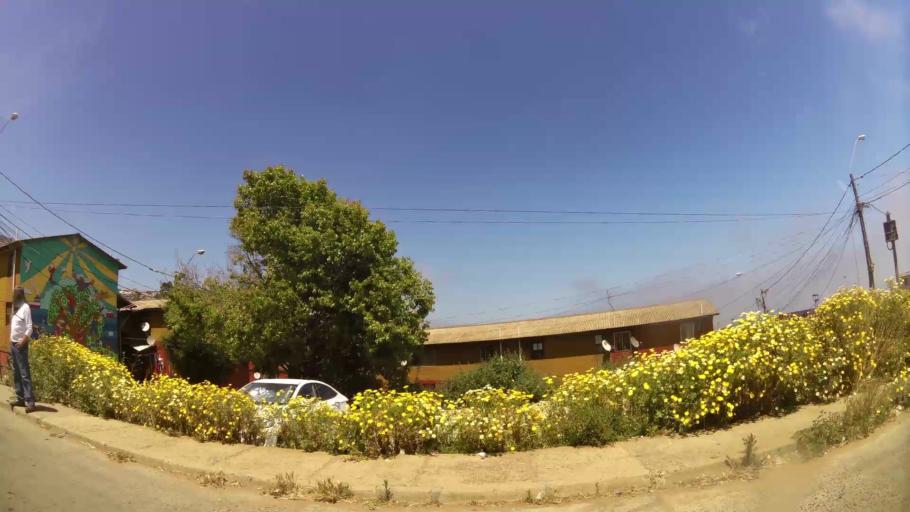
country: CL
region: Valparaiso
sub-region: Provincia de Valparaiso
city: Valparaiso
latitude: -33.0310
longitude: -71.6506
